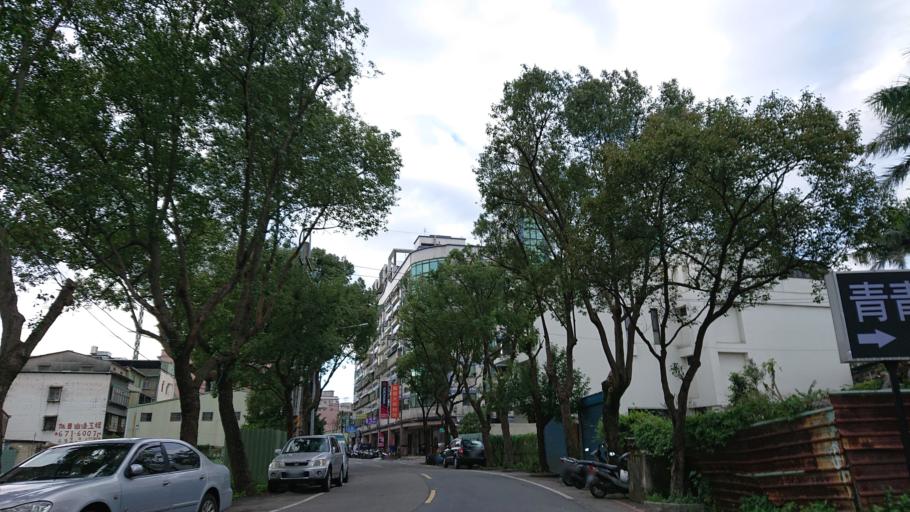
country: TW
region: Taiwan
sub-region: Taoyuan
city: Taoyuan
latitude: 24.9319
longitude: 121.3787
